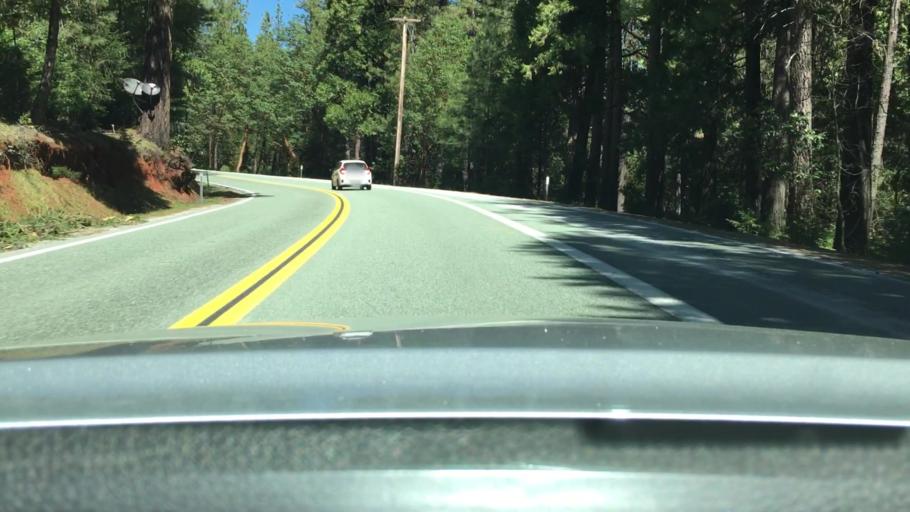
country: US
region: California
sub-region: Amador County
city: Pioneer
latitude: 38.4662
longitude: -120.5273
